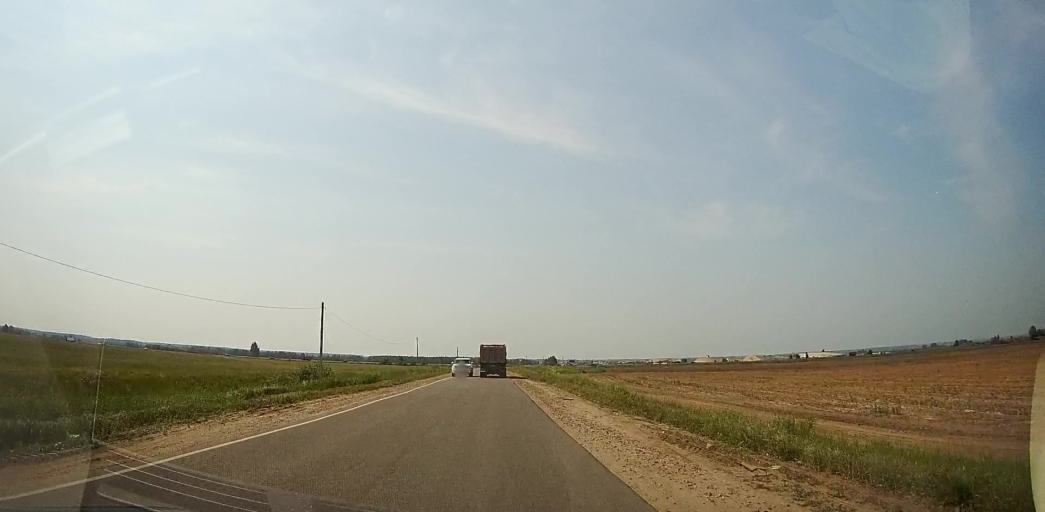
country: RU
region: Moskovskaya
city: Malyshevo
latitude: 55.5074
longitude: 38.2970
